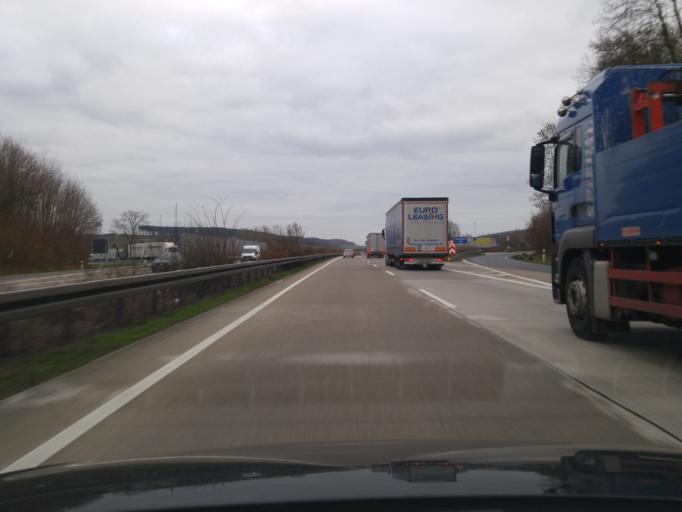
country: DE
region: Lower Saxony
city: Seesen
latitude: 51.8589
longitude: 10.1253
